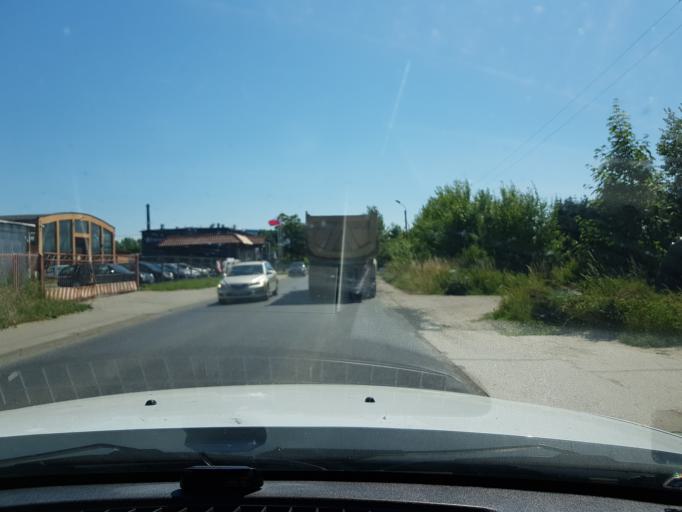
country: PL
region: West Pomeranian Voivodeship
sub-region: Powiat koszalinski
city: Mielno
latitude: 54.2167
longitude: 16.0762
